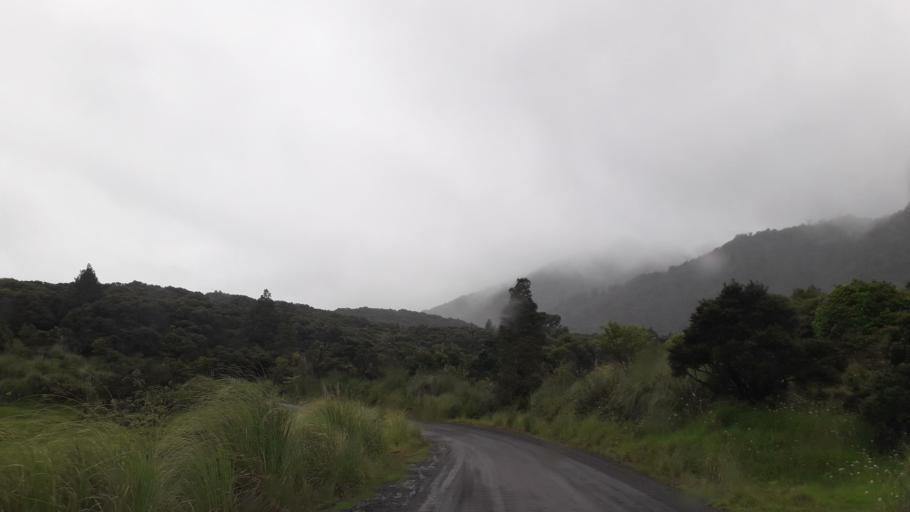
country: NZ
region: Northland
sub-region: Far North District
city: Kaitaia
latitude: -35.4071
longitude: 173.3639
